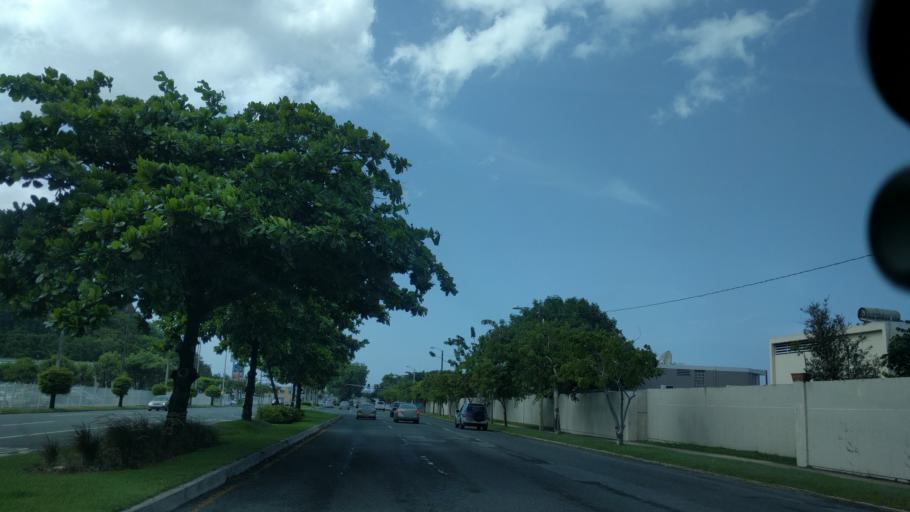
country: PR
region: Bayamon
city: Bayamon
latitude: 18.4116
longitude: -66.1598
